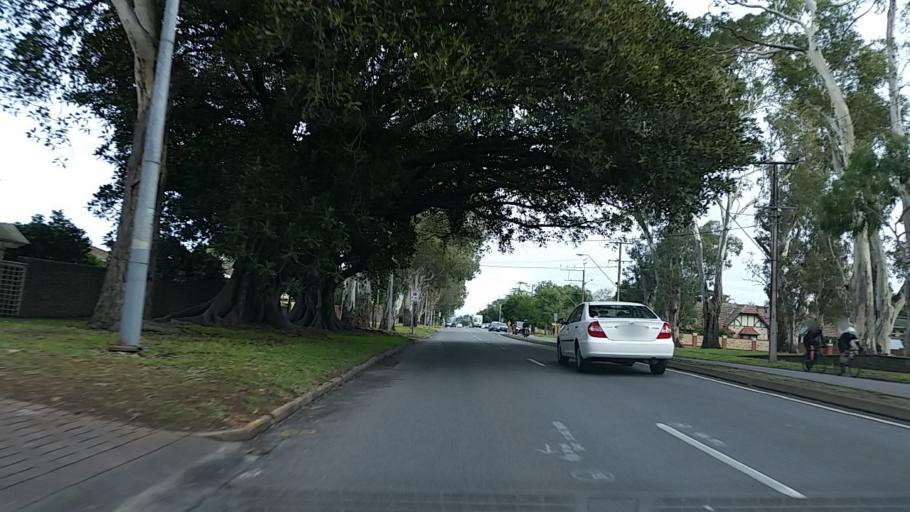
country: AU
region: South Australia
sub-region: Burnside
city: Hazelwood Park
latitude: -34.9385
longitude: 138.6573
